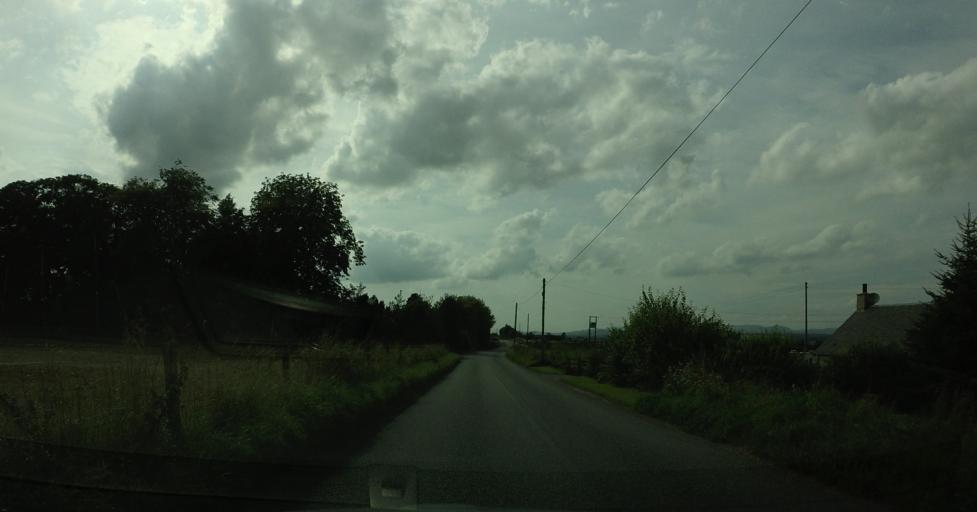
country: GB
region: Scotland
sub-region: Perth and Kinross
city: Methven
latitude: 56.3943
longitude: -3.5554
